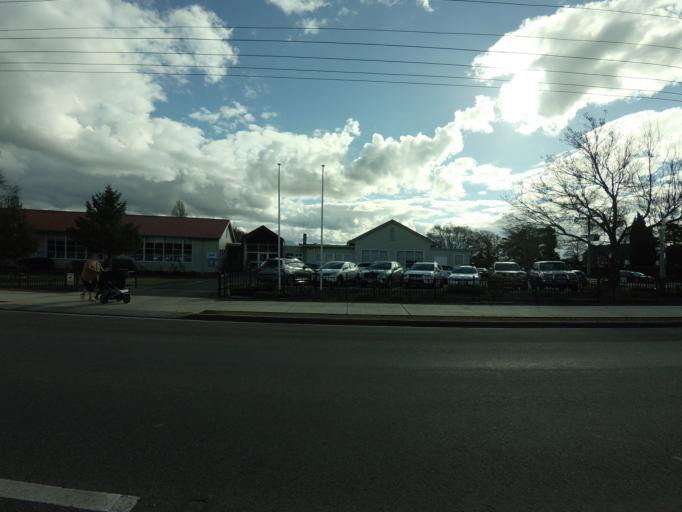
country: AU
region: Tasmania
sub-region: Northern Midlands
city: Longford
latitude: -41.6903
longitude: 147.0794
